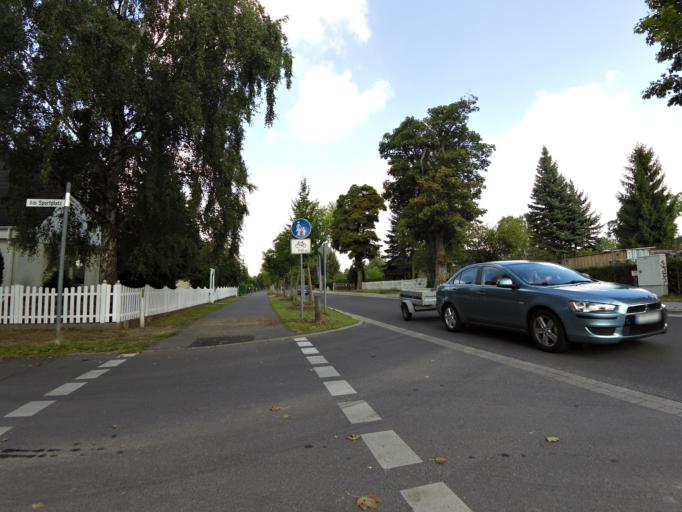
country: DE
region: Berlin
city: Lichtenrade
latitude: 52.3604
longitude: 13.4048
